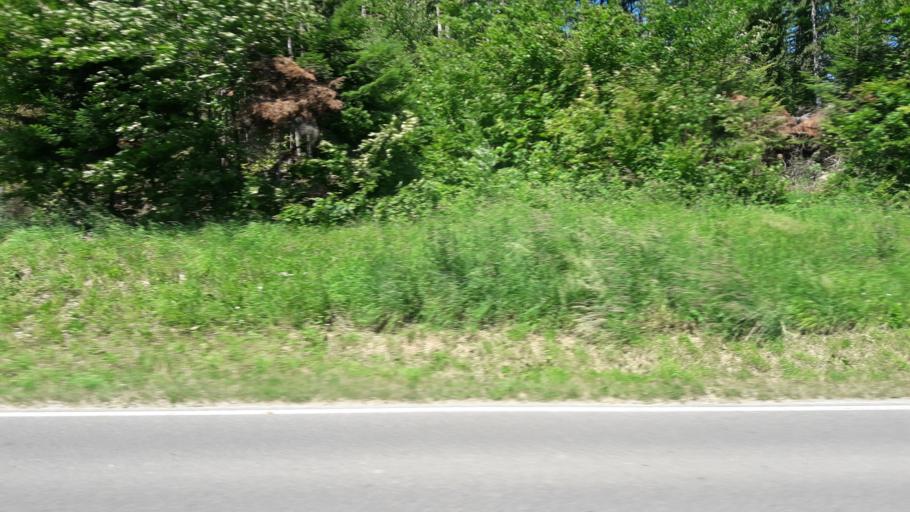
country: CH
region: Bern
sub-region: Seeland District
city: Tauffelen
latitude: 47.0539
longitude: 7.1824
